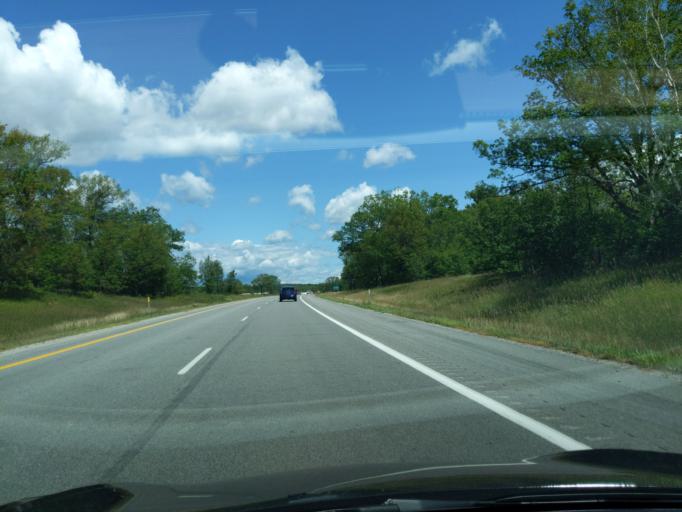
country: US
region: Michigan
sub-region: Clare County
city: Harrison
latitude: 43.9388
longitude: -84.7833
